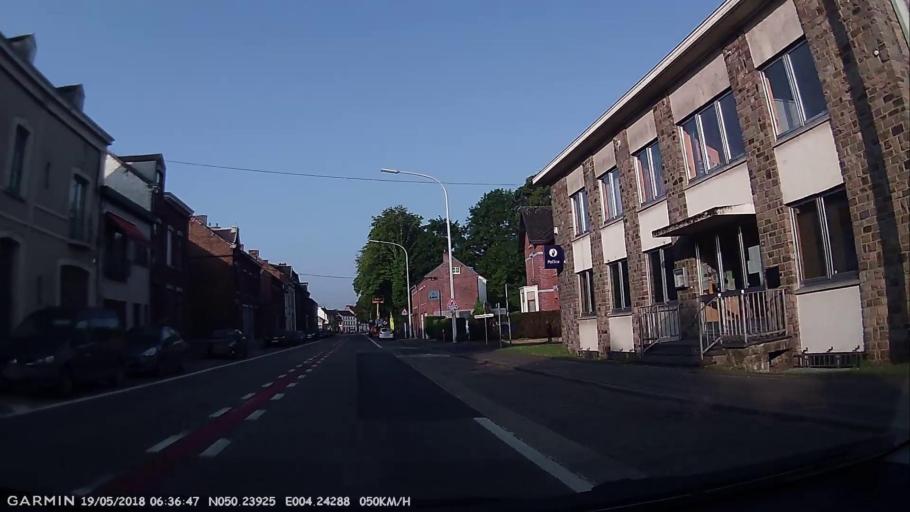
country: BE
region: Wallonia
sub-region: Province du Hainaut
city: Beaumont
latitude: 50.2392
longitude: 4.2427
